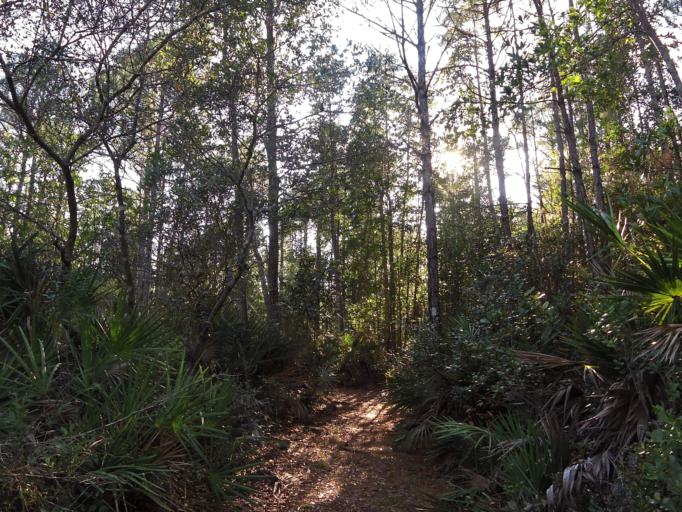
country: US
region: Florida
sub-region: Duval County
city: Atlantic Beach
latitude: 30.4769
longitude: -81.4926
